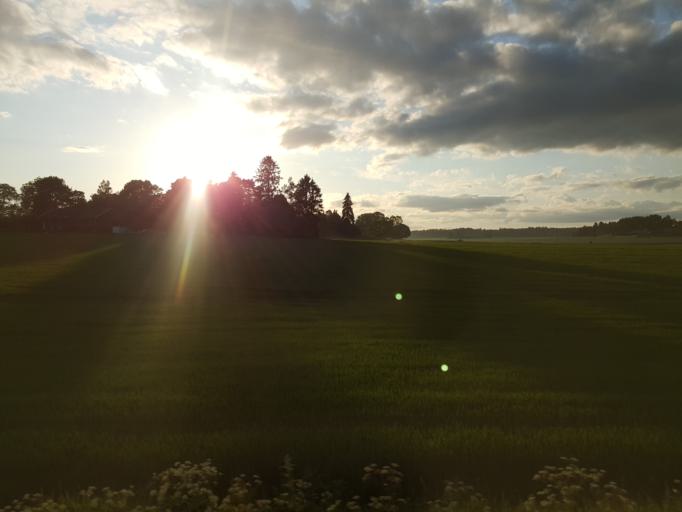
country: SE
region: Uppsala
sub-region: Uppsala Kommun
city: Vattholma
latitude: 59.9384
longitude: 17.8228
